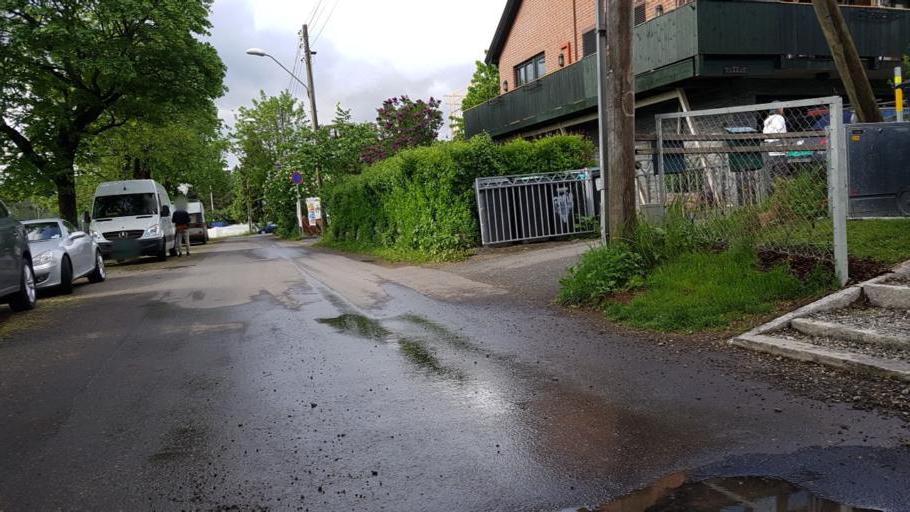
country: NO
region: Oslo
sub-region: Oslo
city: Oslo
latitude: 59.9428
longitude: 10.7886
